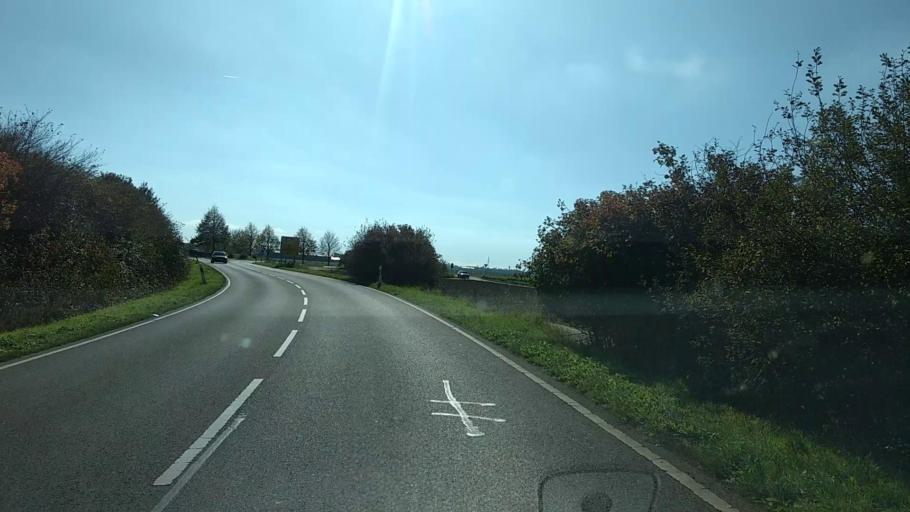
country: DE
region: North Rhine-Westphalia
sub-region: Regierungsbezirk Koln
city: Bergheim
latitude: 50.9120
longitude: 6.6598
